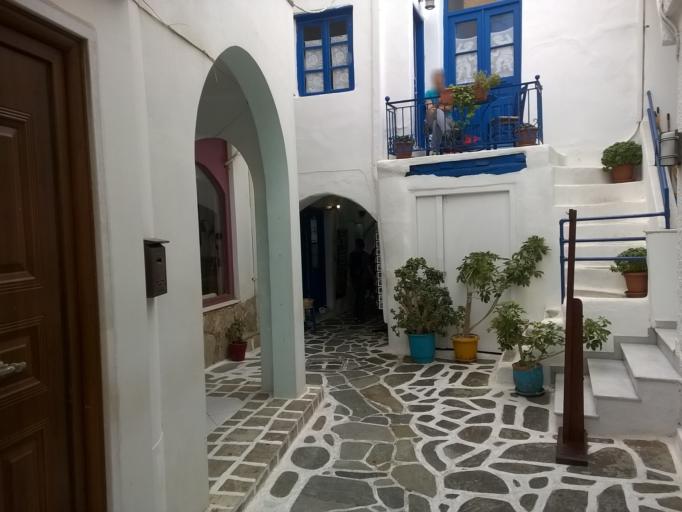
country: GR
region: South Aegean
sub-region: Nomos Kykladon
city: Naxos
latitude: 37.1071
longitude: 25.3753
